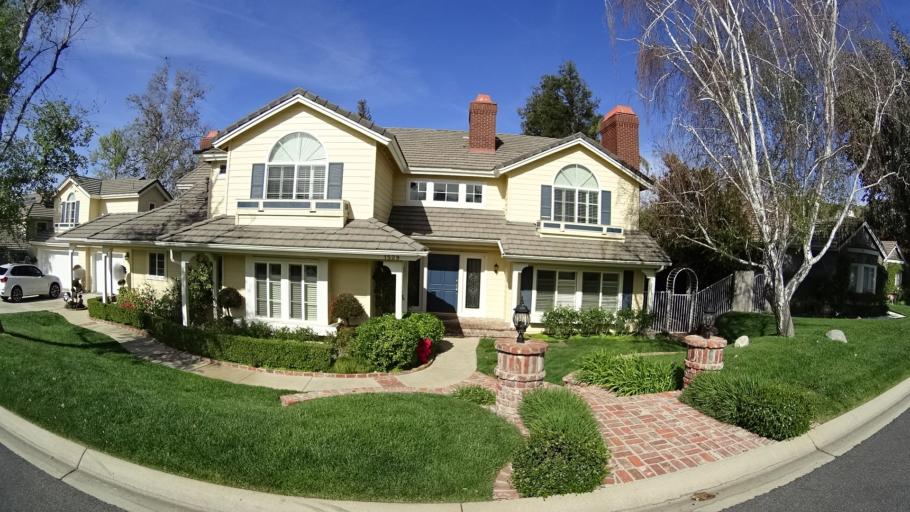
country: US
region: California
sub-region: Ventura County
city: Oak Park
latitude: 34.1917
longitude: -118.7860
